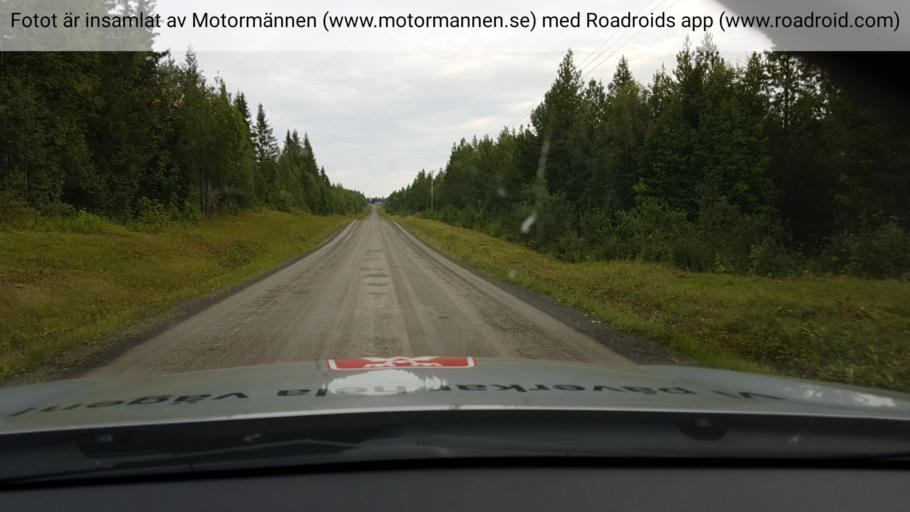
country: SE
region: Jaemtland
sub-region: OEstersunds Kommun
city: Lit
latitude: 63.6244
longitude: 14.9766
